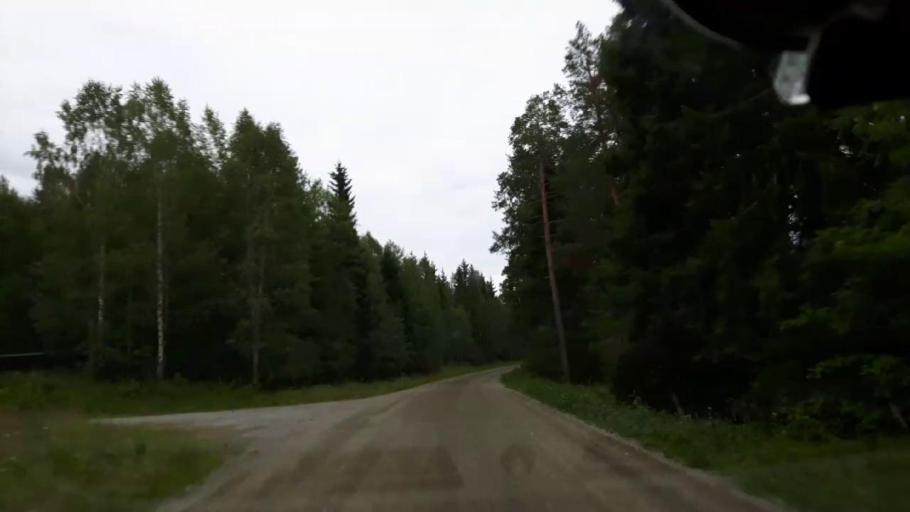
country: SE
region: Jaemtland
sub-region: Braecke Kommun
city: Braecke
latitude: 62.9861
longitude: 15.3895
